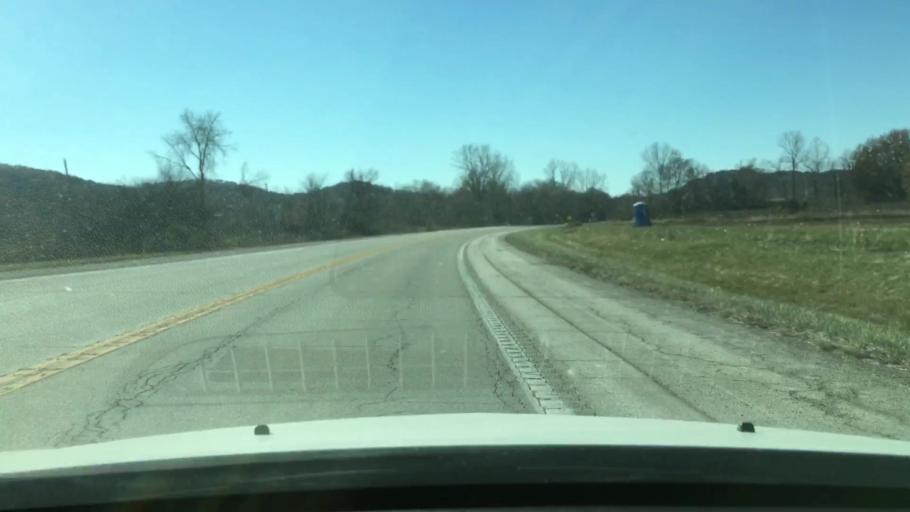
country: US
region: Missouri
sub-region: Pike County
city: Louisiana
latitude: 39.4203
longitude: -91.0879
